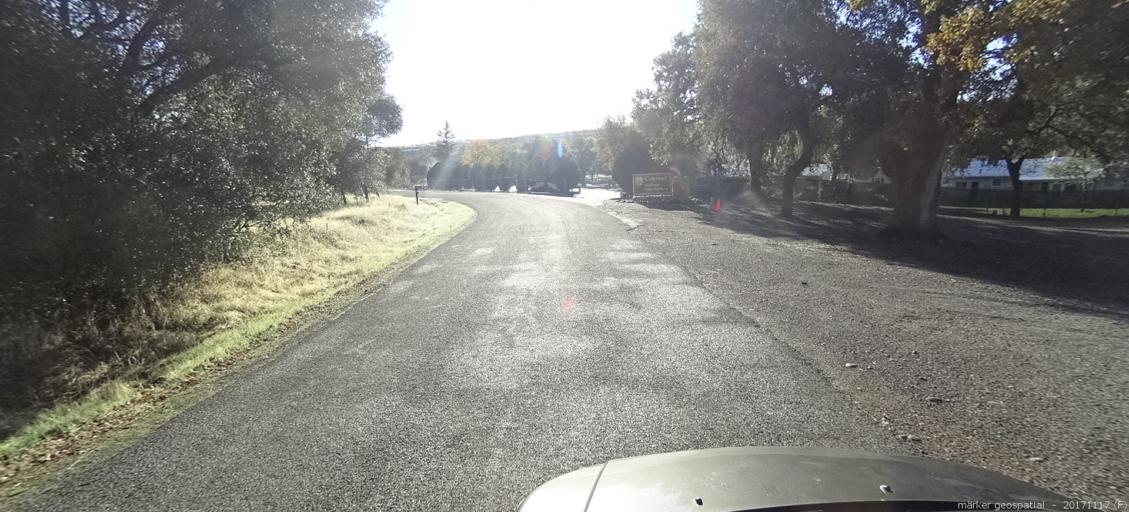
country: US
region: California
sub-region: Shasta County
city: Cottonwood
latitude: 40.4022
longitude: -122.1456
